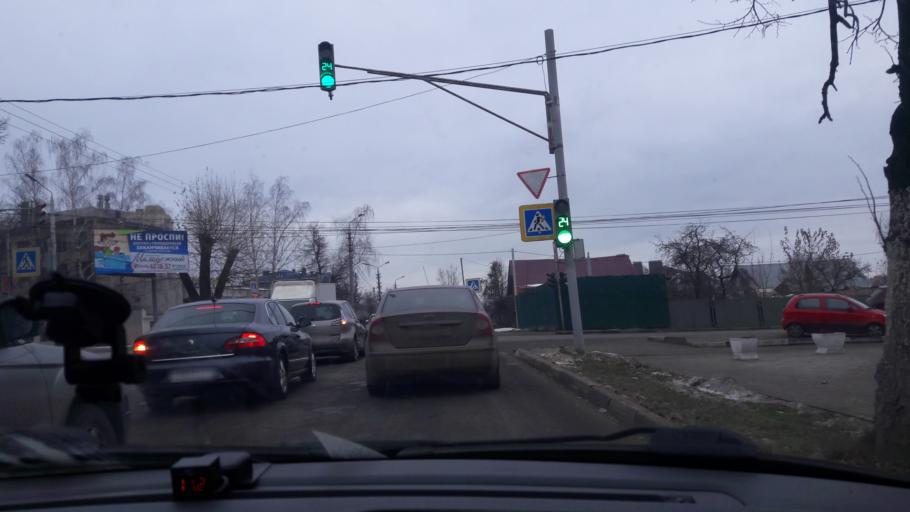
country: RU
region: Tula
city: Tula
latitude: 54.2062
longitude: 37.6535
